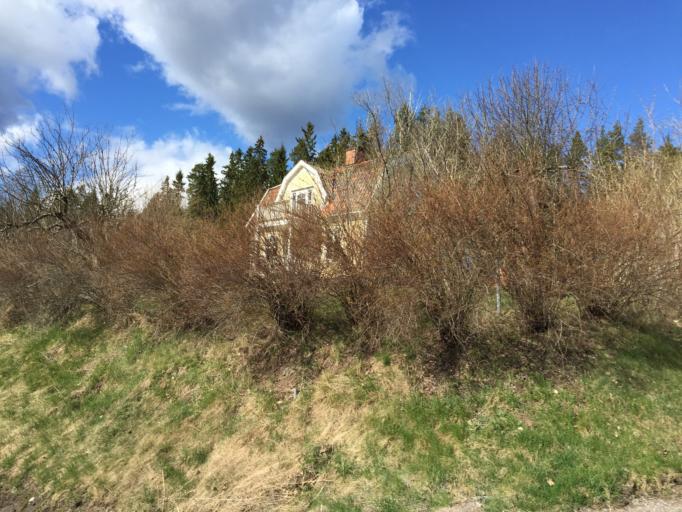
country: SE
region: OEstergoetland
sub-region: Norrkopings Kommun
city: Svartinge
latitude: 58.8267
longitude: 15.9440
